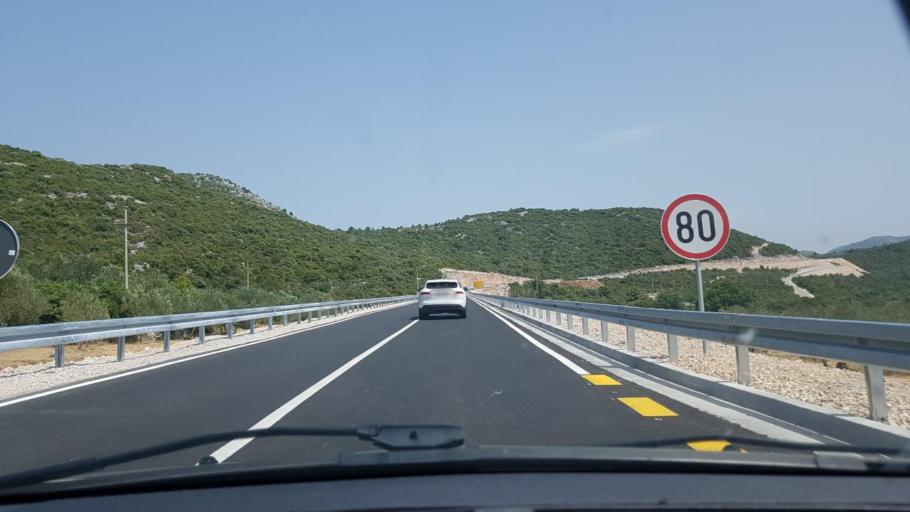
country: HR
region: Dubrovacko-Neretvanska
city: Ston
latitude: 42.9524
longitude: 17.7519
